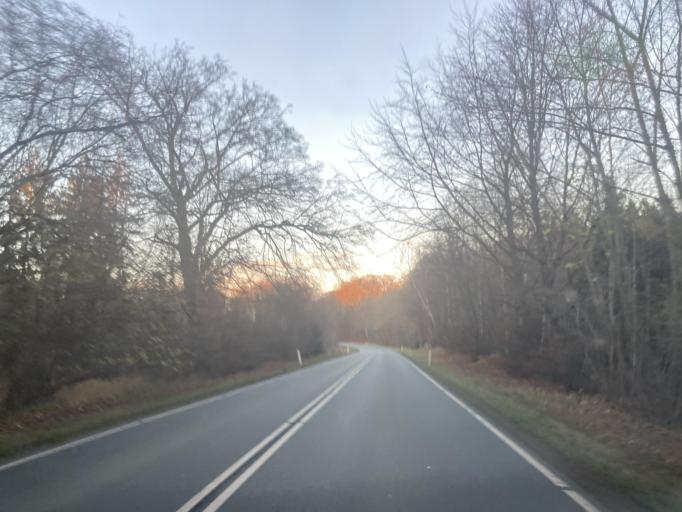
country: DK
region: Capital Region
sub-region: Gribskov Kommune
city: Graested
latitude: 56.0379
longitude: 12.2817
